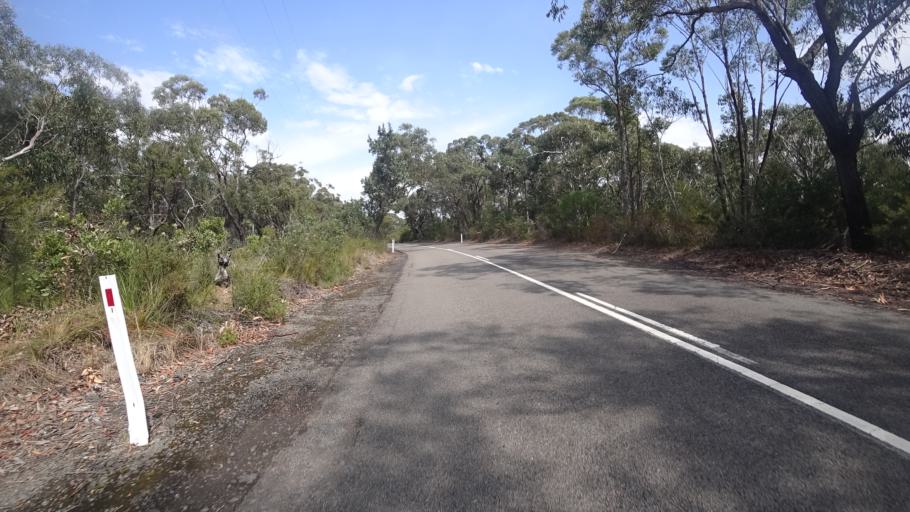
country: AU
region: New South Wales
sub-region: Hornsby Shire
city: Mount Colah
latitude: -33.6771
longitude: 151.1287
